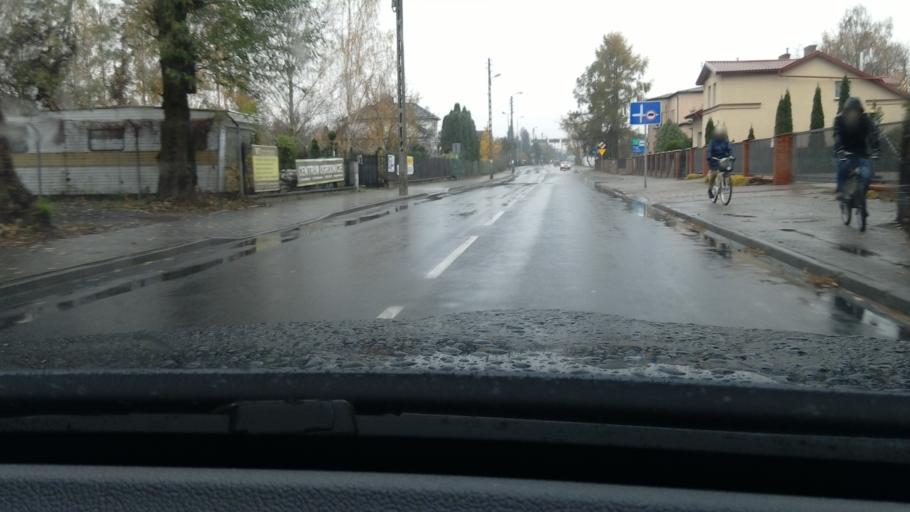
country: PL
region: Lodz Voivodeship
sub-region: Skierniewice
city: Skierniewice
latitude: 51.9547
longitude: 20.1341
